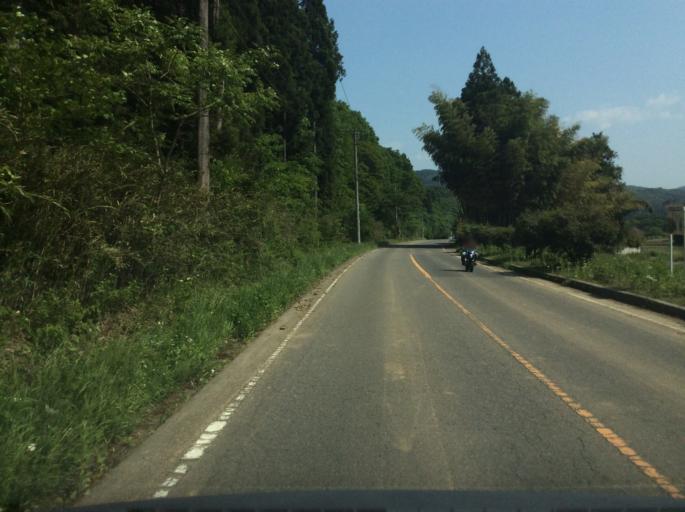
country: JP
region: Tochigi
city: Kuroiso
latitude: 37.0681
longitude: 140.2294
